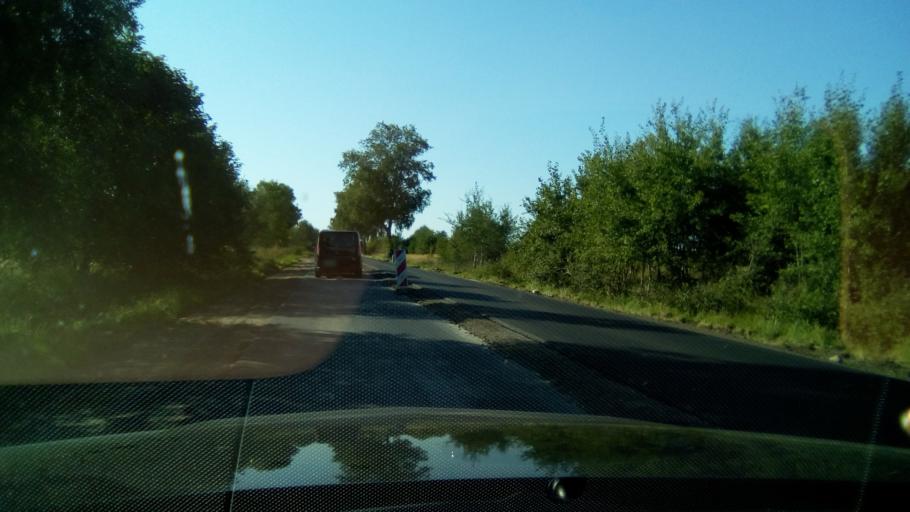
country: PL
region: West Pomeranian Voivodeship
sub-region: Powiat gryficki
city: Ploty
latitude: 53.8100
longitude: 15.2174
